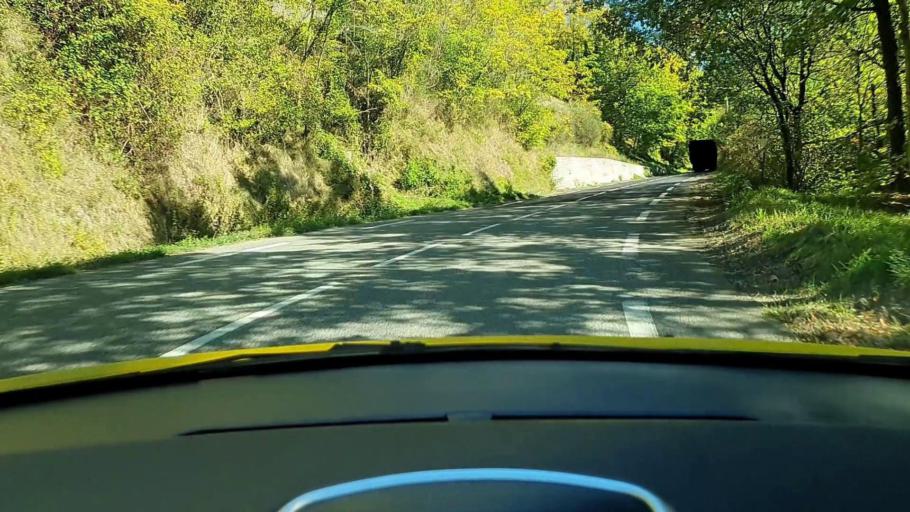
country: FR
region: Languedoc-Roussillon
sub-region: Departement du Gard
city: Le Vigan
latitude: 43.9774
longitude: 3.4608
